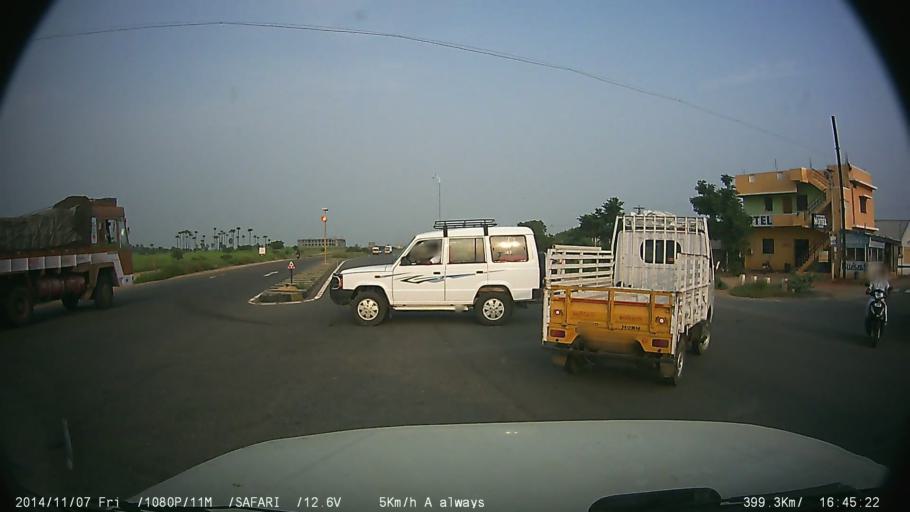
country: IN
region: Tamil Nadu
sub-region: Erode
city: Perundurai
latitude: 11.2887
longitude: 77.5651
